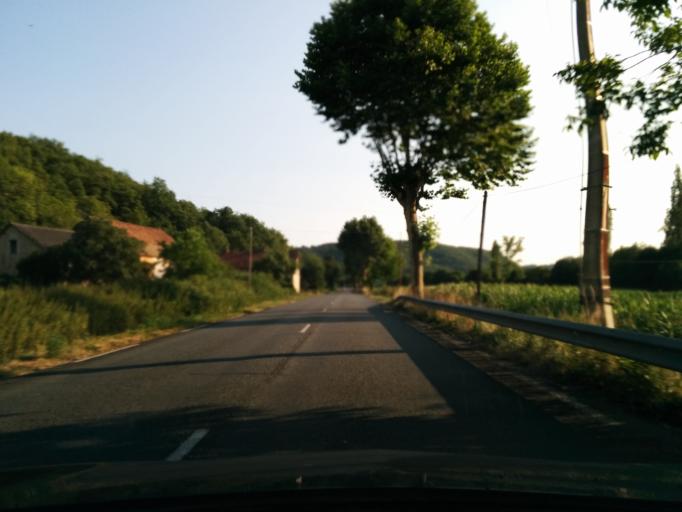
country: FR
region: Midi-Pyrenees
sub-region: Departement du Lot
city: Le Vigan
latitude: 44.6791
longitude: 1.4803
